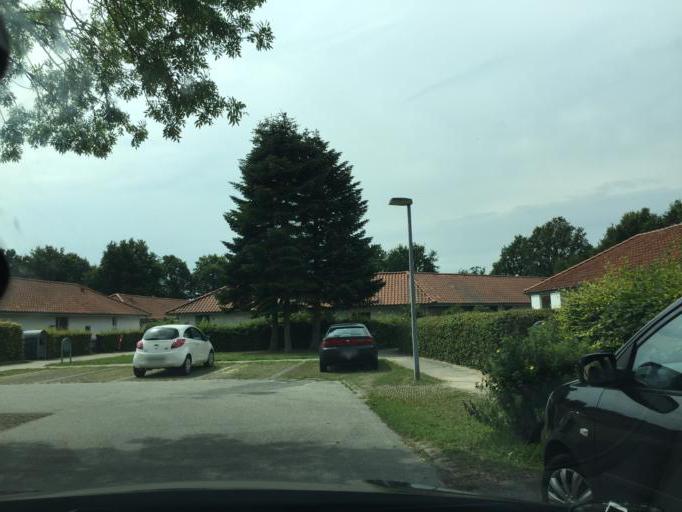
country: DK
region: South Denmark
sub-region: Odense Kommune
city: Neder Holluf
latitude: 55.3635
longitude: 10.4414
